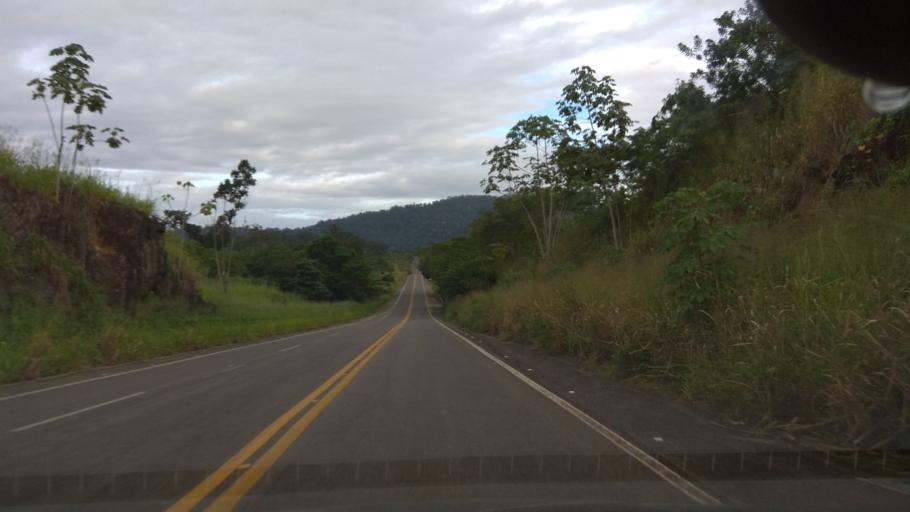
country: BR
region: Bahia
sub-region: Ubaitaba
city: Ubaitaba
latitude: -14.2472
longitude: -39.3587
